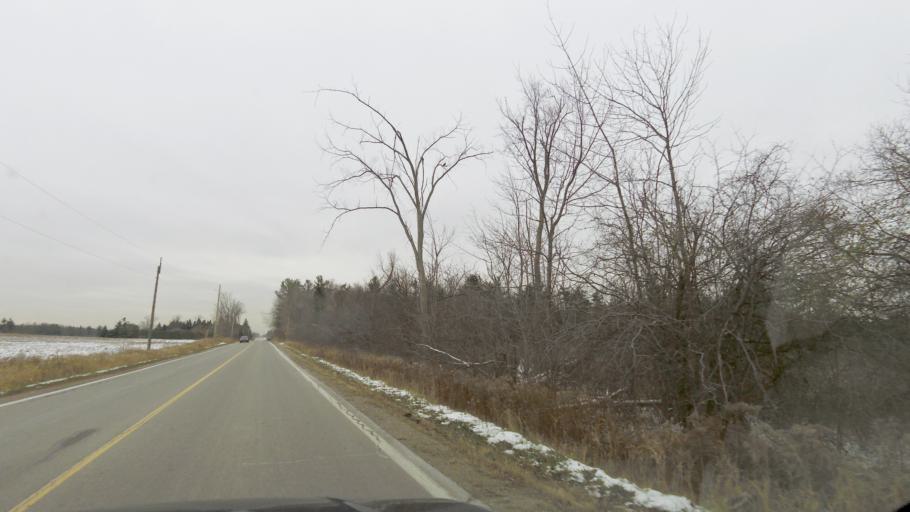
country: CA
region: Ontario
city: Vaughan
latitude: 43.8614
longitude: -79.5914
